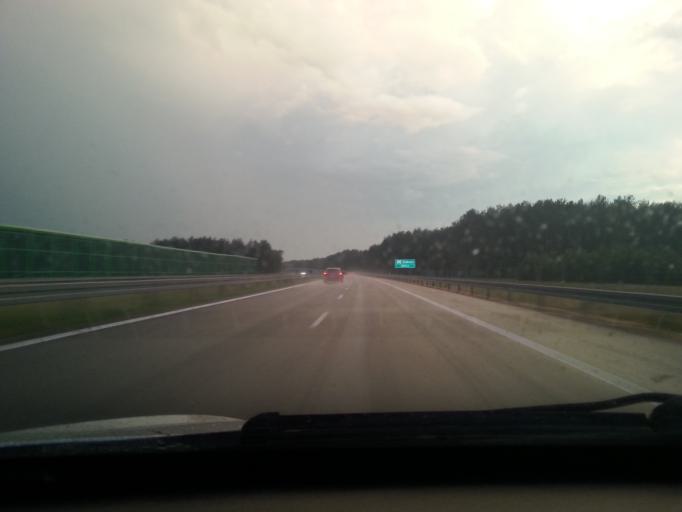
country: PL
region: Lodz Voivodeship
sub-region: Powiat pabianicki
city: Dobron
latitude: 51.6688
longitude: 19.2856
